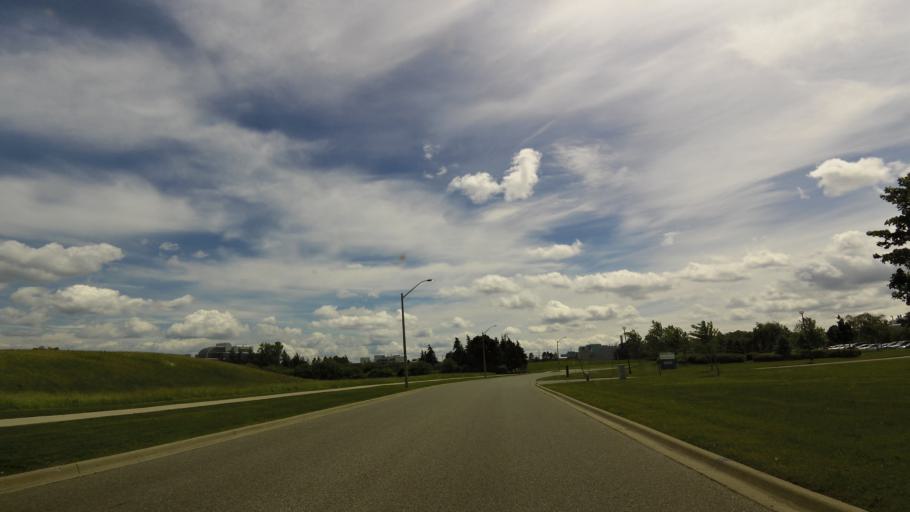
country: CA
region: Ontario
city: Mississauga
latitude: 43.5149
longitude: -79.6634
